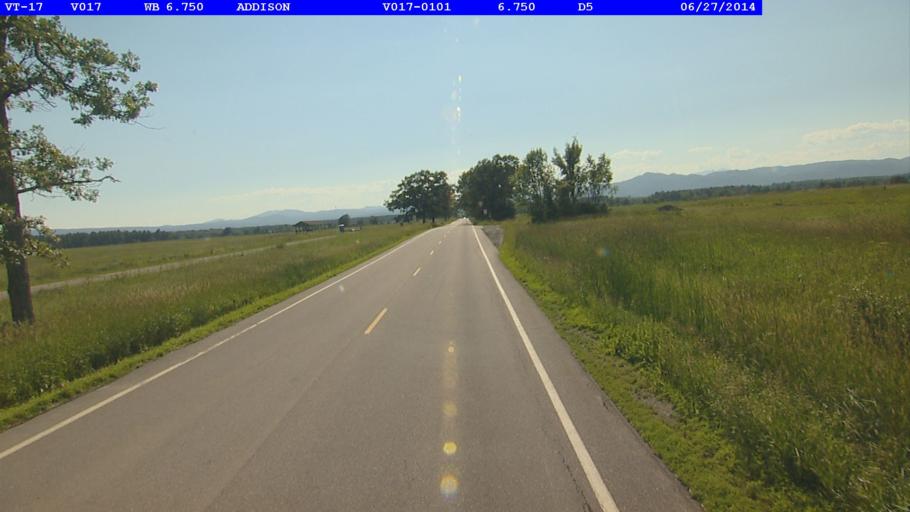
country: US
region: Vermont
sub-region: Addison County
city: Vergennes
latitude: 44.0858
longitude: -73.3348
